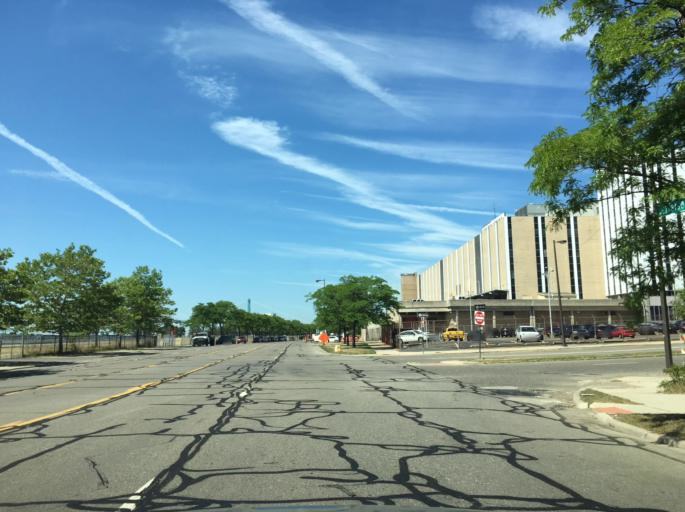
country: US
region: Michigan
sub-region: Wayne County
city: Detroit
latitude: 42.3245
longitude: -83.0582
